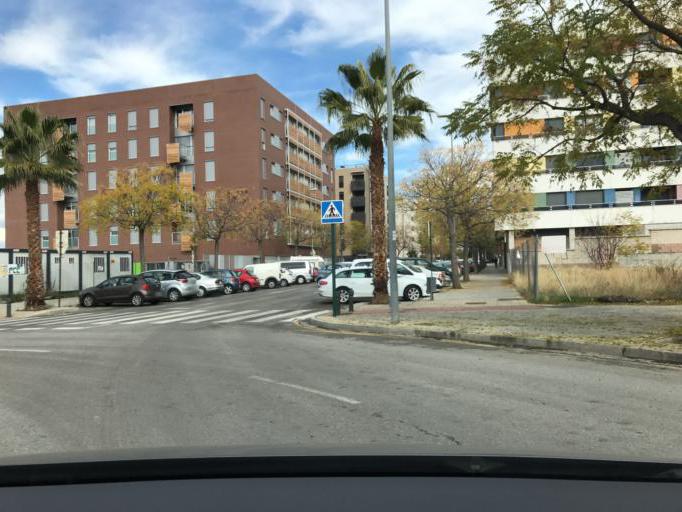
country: ES
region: Andalusia
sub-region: Provincia de Granada
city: Armilla
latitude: 37.1571
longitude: -3.6106
